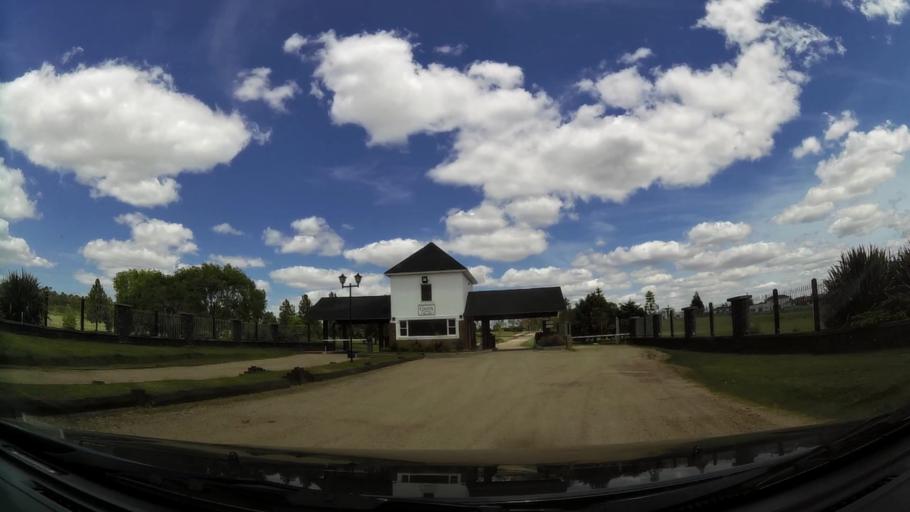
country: UY
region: Canelones
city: Colonia Nicolich
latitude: -34.7909
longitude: -56.0157
